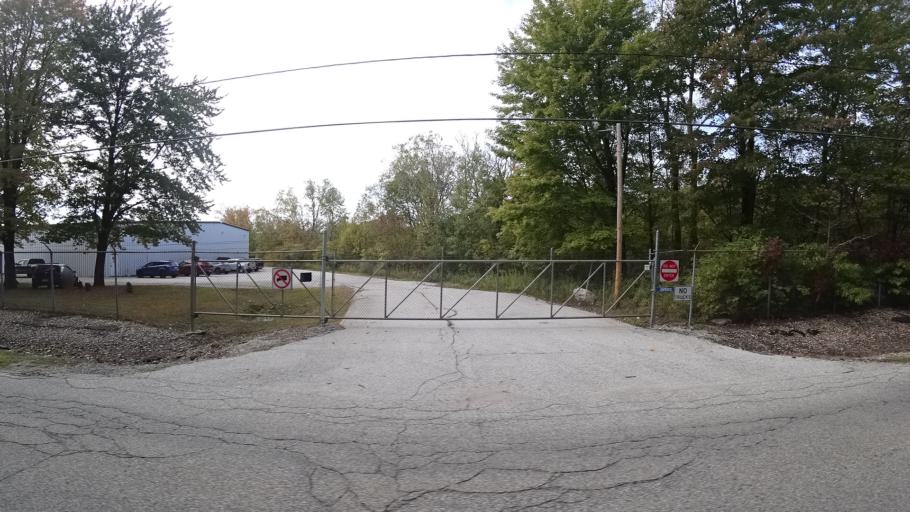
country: US
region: Indiana
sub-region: LaPorte County
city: Long Beach
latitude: 41.7193
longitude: -86.8407
